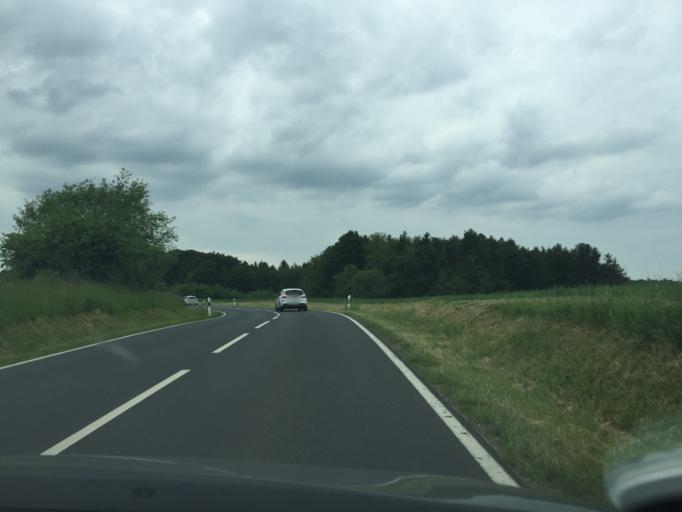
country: DE
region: Bavaria
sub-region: Regierungsbezirk Unterfranken
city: Goldbach
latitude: 50.0265
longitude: 9.1817
